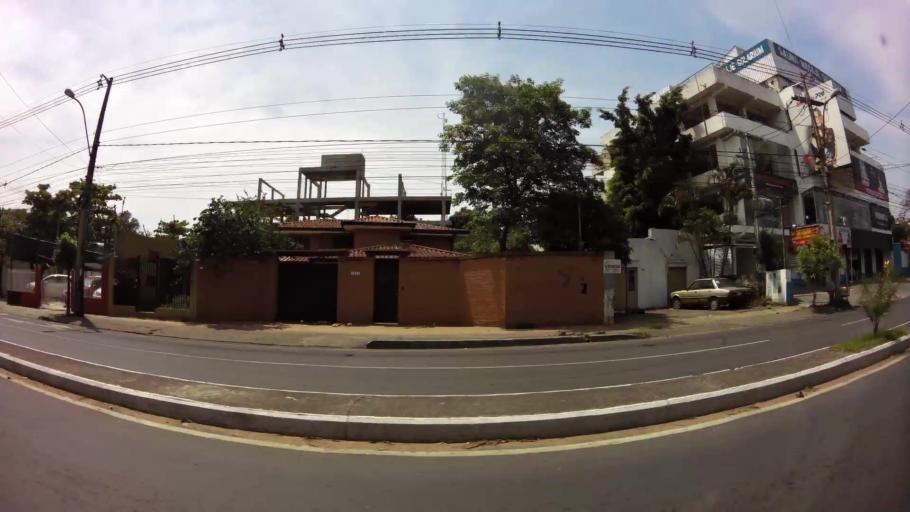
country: PY
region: Asuncion
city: Asuncion
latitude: -25.2986
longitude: -57.5935
